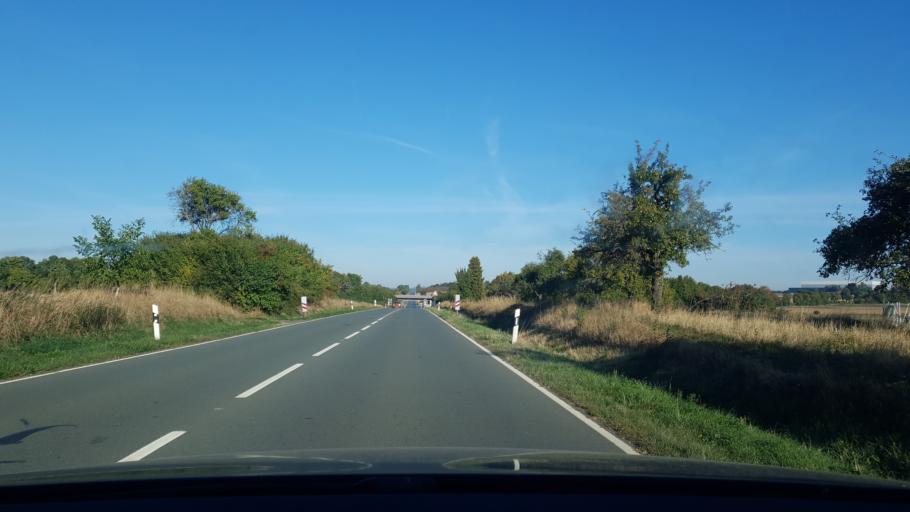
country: DE
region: Hesse
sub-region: Regierungsbezirk Darmstadt
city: Butzbach
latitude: 50.4625
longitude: 8.6455
